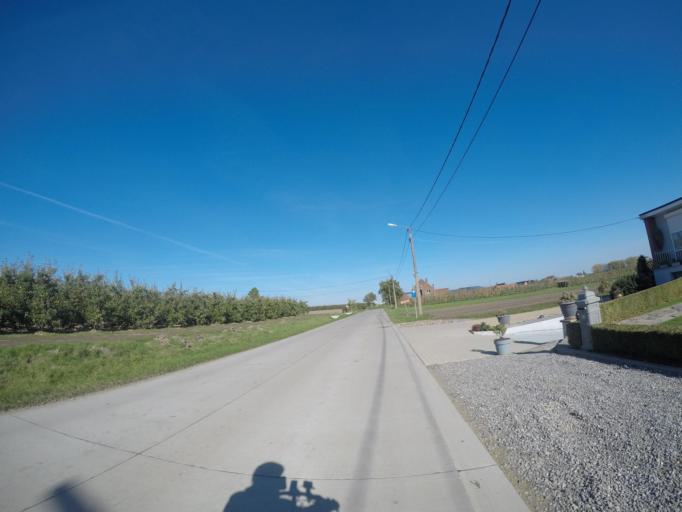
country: BE
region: Flanders
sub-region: Provincie Limburg
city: Alken
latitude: 50.8878
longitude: 5.2496
